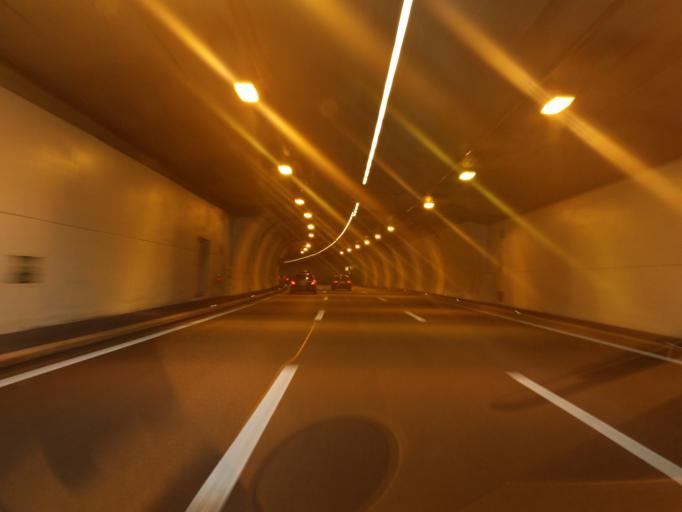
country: CH
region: Zurich
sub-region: Bezirk Dietikon
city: Birmensdorf
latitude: 47.3421
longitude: 8.4525
